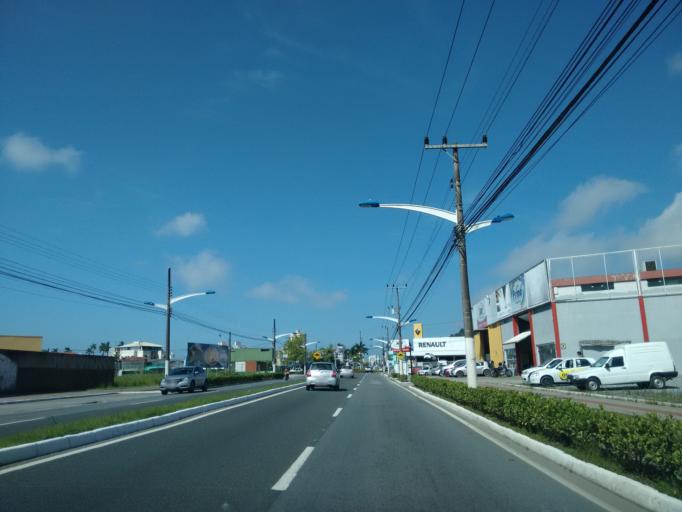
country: BR
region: Santa Catarina
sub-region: Itajai
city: Itajai
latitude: -26.9253
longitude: -48.6787
